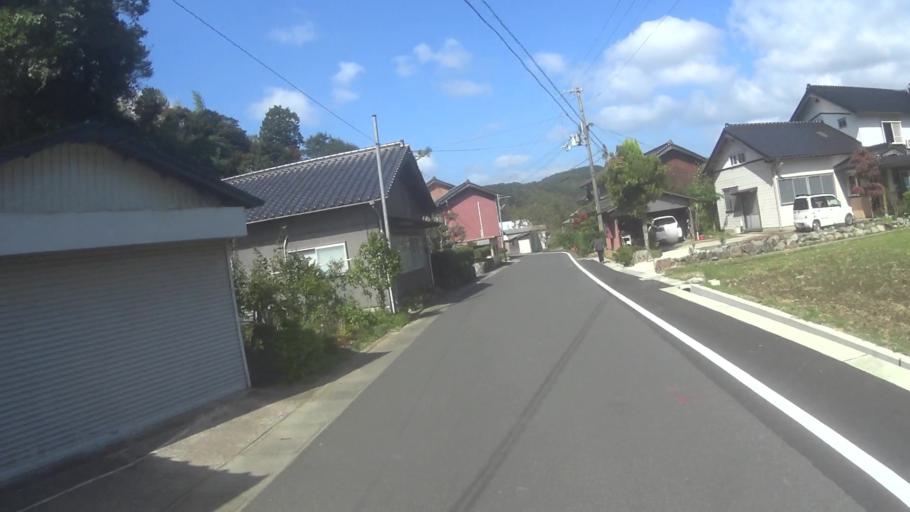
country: JP
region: Kyoto
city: Miyazu
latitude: 35.7113
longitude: 135.1154
